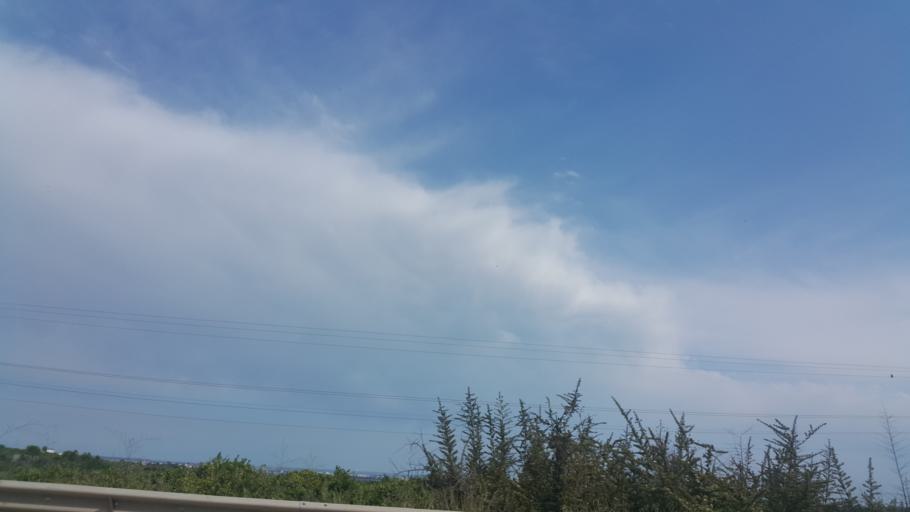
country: TR
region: Mersin
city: Mercin
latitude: 36.8950
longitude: 34.6522
